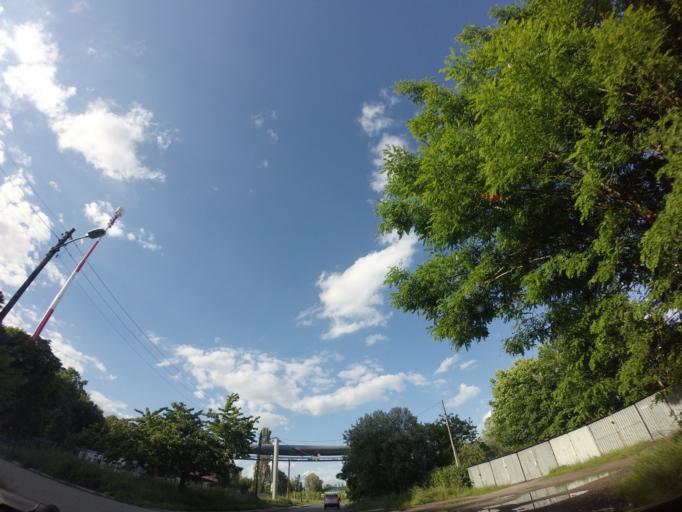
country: PL
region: West Pomeranian Voivodeship
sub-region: Szczecin
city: Szczecin
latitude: 53.3949
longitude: 14.5303
